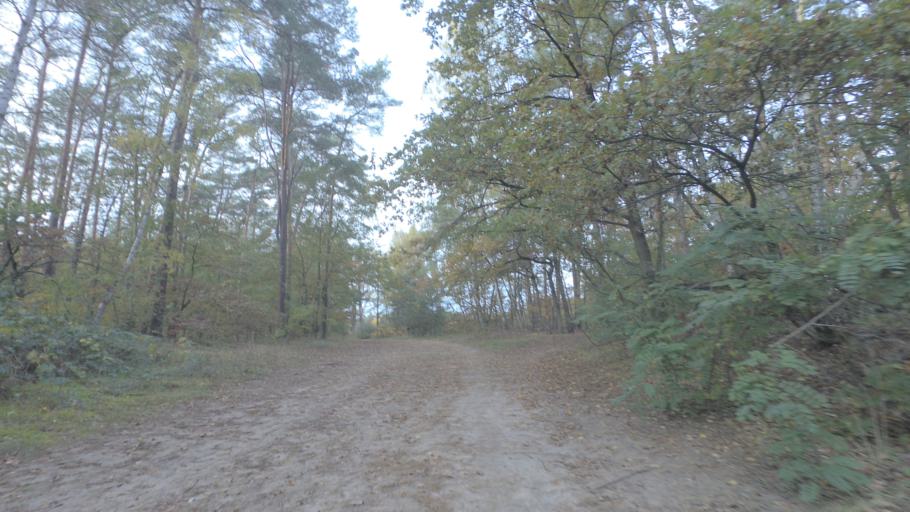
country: DE
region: Brandenburg
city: Ludwigsfelde
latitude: 52.3063
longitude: 13.2377
